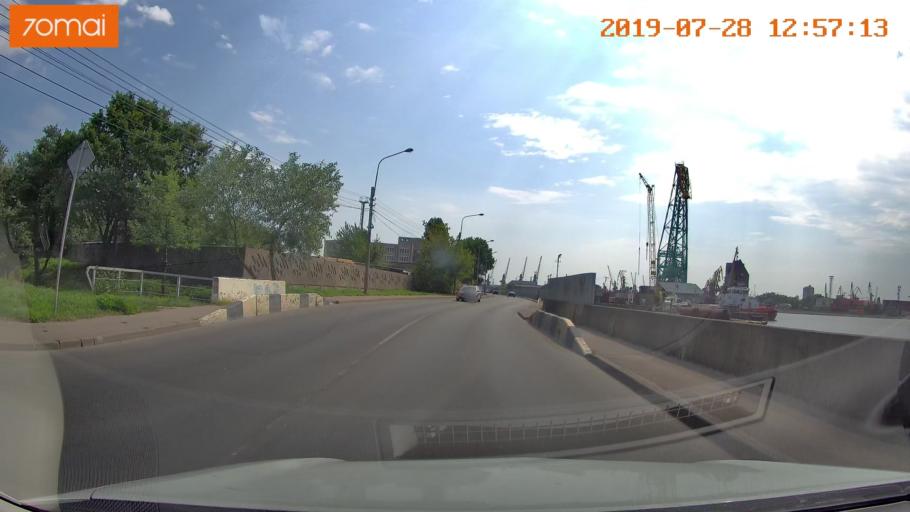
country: RU
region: Kaliningrad
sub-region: Gorod Kaliningrad
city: Kaliningrad
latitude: 54.7077
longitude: 20.4672
